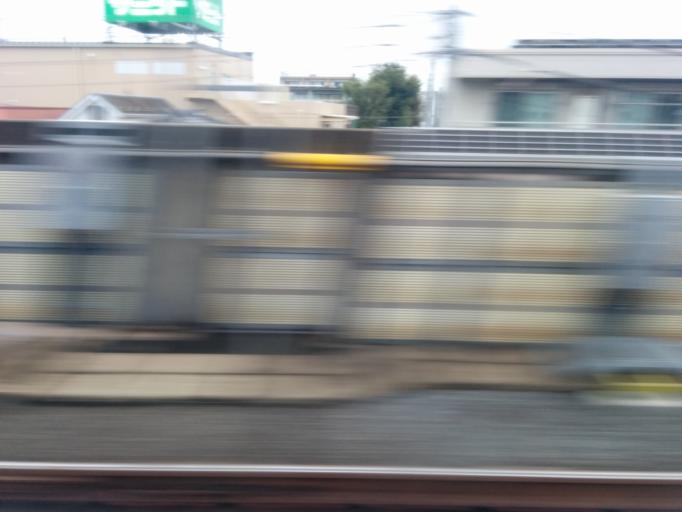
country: JP
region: Tokyo
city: Tokyo
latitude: 35.6556
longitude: 139.6516
